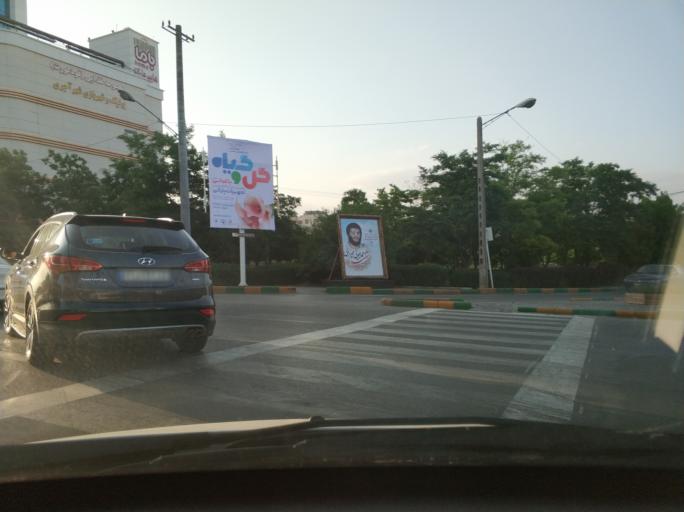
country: IR
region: Razavi Khorasan
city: Mashhad
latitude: 36.3389
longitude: 59.5536
